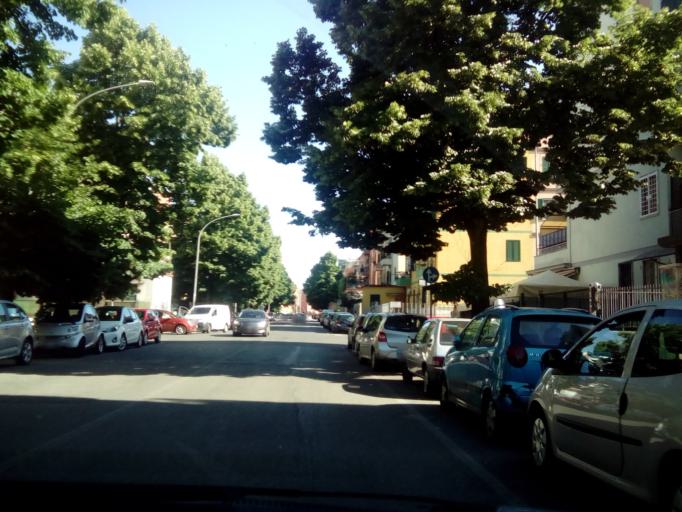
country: IT
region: Latium
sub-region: Citta metropolitana di Roma Capitale
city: Rome
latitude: 41.8901
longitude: 12.5667
